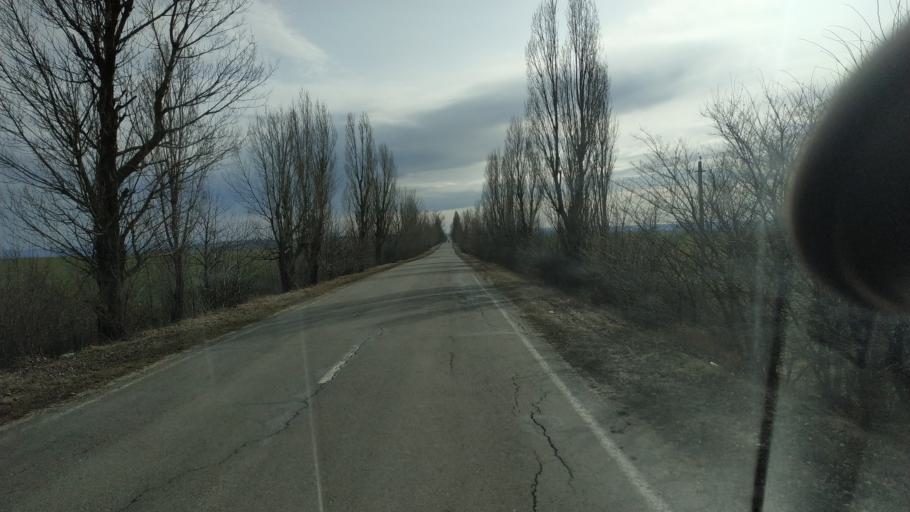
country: MD
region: Telenesti
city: Cocieri
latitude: 47.3760
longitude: 29.0431
